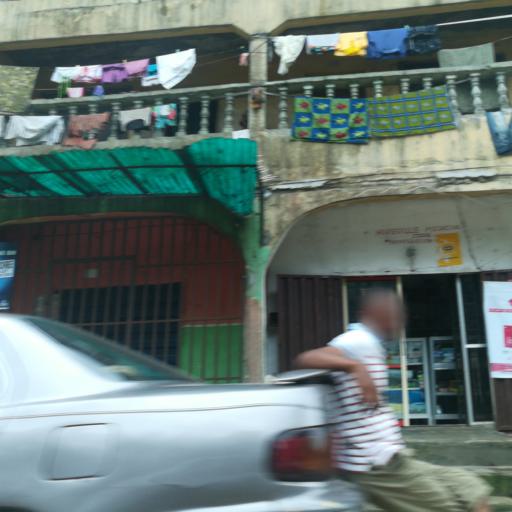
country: NG
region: Rivers
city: Port Harcourt
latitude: 4.8108
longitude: 7.0483
